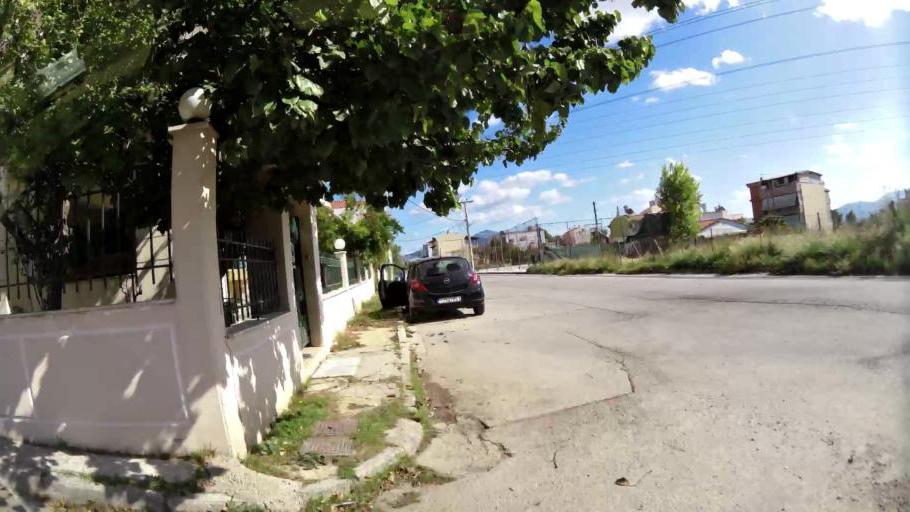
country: GR
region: Attica
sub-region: Nomarchia Anatolikis Attikis
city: Acharnes
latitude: 38.1048
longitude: 23.7402
